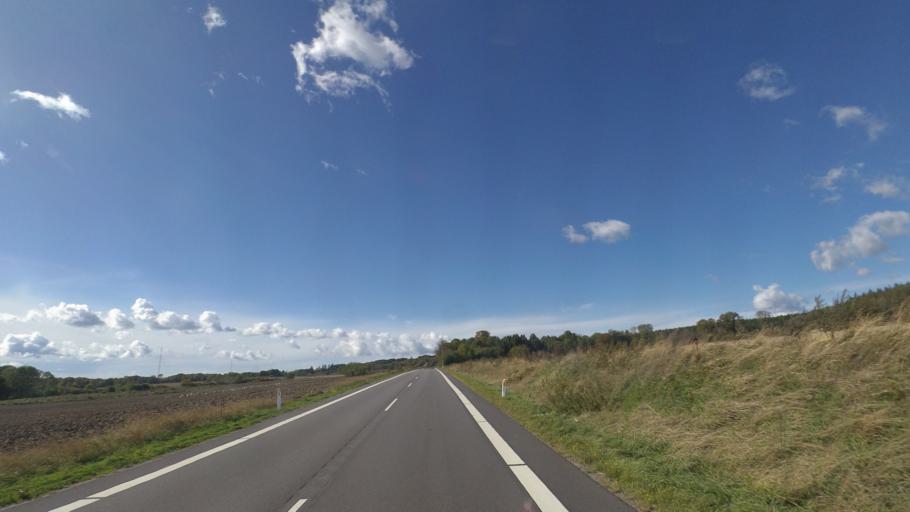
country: DK
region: Capital Region
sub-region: Bornholm Kommune
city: Nexo
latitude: 55.0621
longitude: 15.0345
